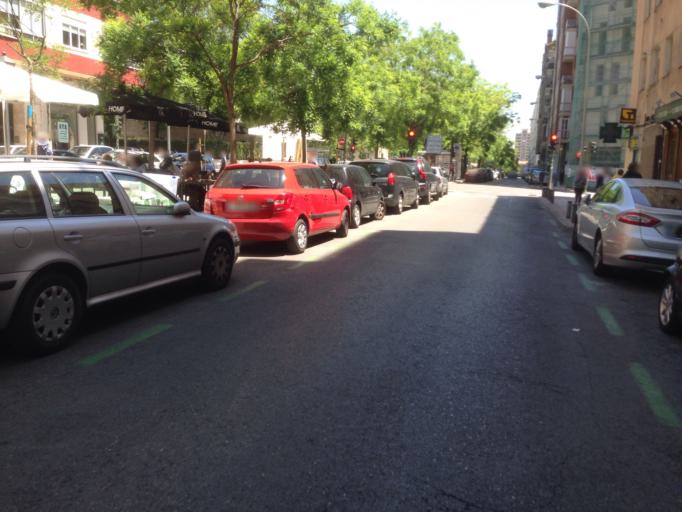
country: ES
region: Madrid
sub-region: Provincia de Madrid
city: Retiro
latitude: 40.4182
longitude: -3.6737
